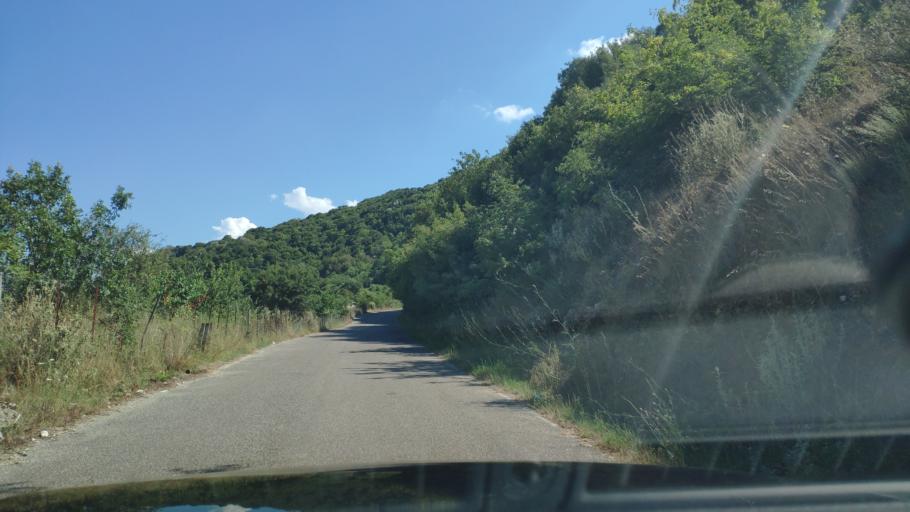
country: GR
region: West Greece
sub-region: Nomos Aitolias kai Akarnanias
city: Katouna
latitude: 38.8263
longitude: 21.0997
